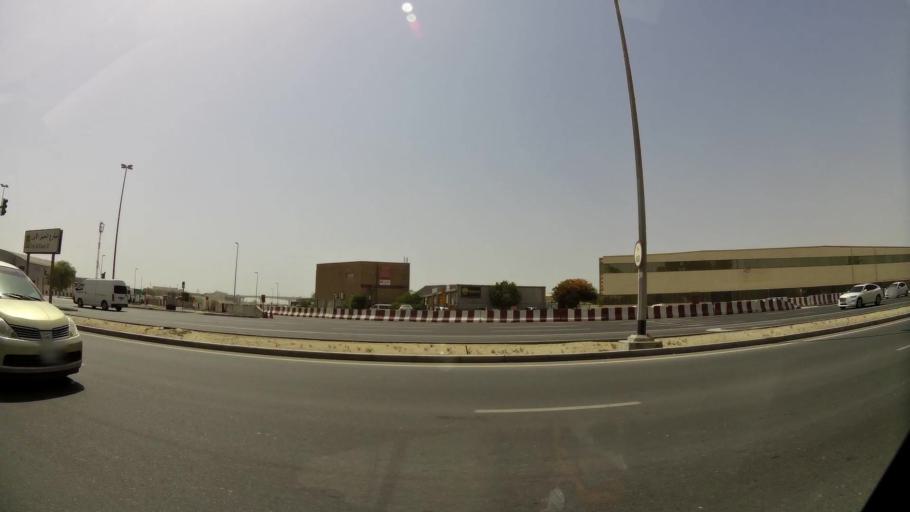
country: AE
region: Dubai
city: Dubai
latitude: 25.1613
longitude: 55.2409
